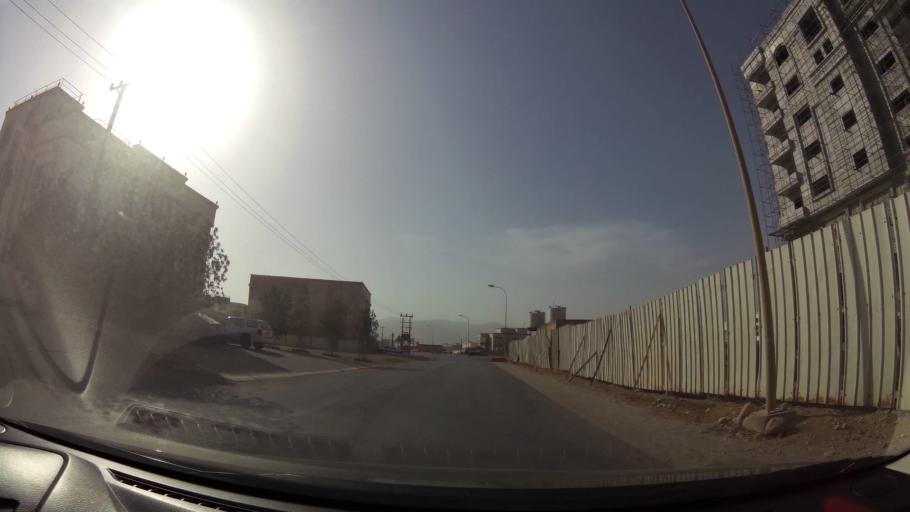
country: OM
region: Zufar
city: Salalah
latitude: 17.0085
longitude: 54.0201
